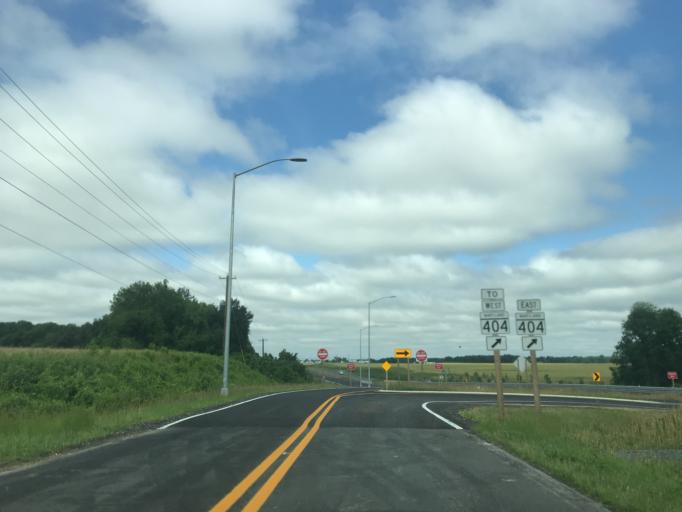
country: US
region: Maryland
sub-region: Caroline County
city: Ridgely
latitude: 38.9232
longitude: -75.9759
